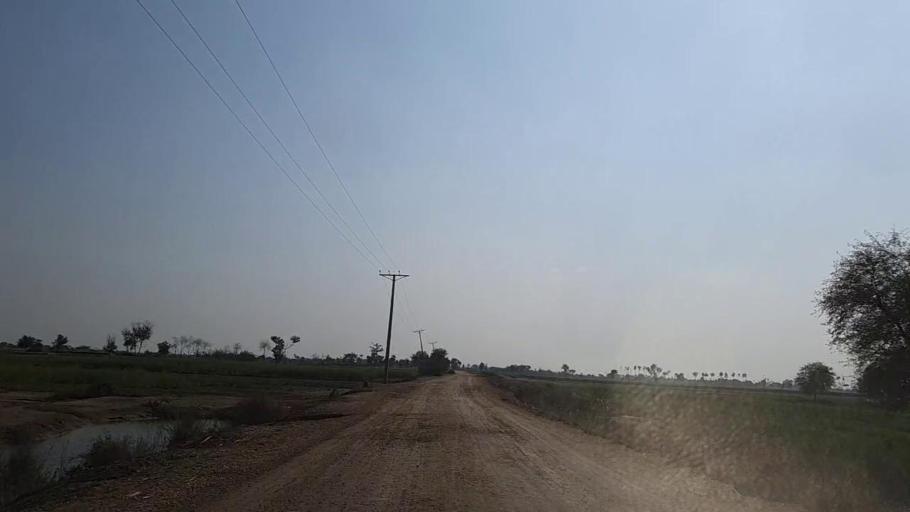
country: PK
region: Sindh
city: Daur
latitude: 26.4608
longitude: 68.2349
